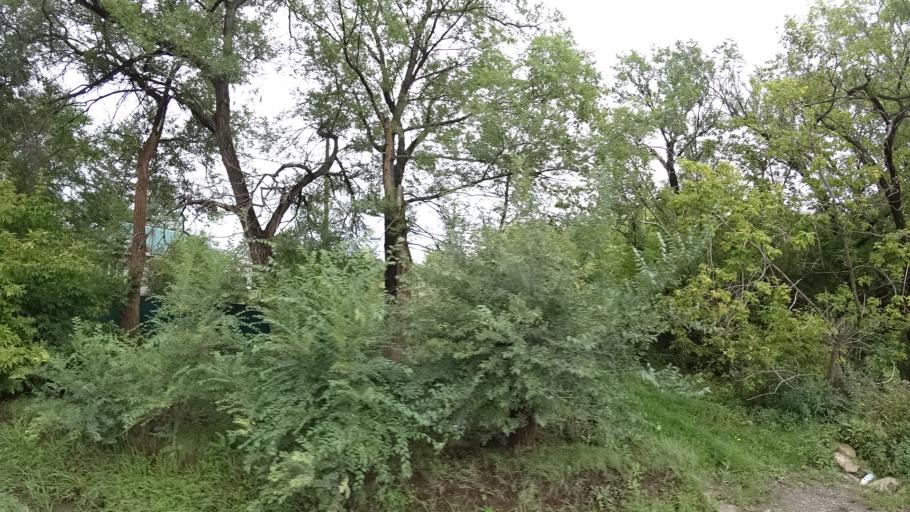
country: RU
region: Primorskiy
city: Chernigovka
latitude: 44.3321
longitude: 132.5674
